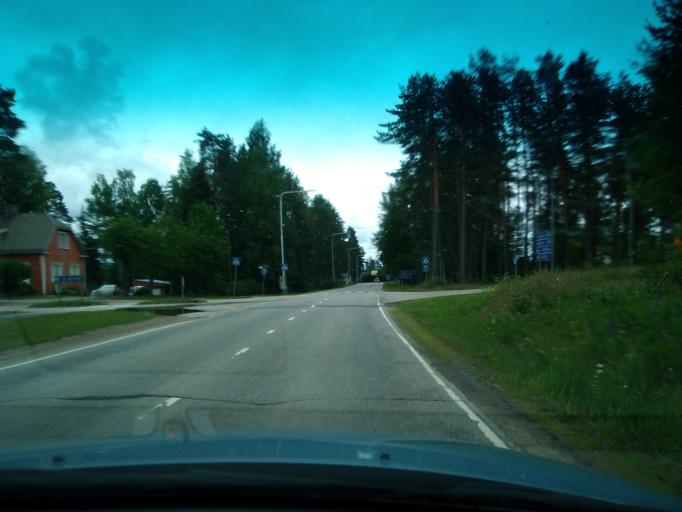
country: FI
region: Central Finland
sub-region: Keuruu
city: Multia
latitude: 62.4115
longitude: 24.7977
